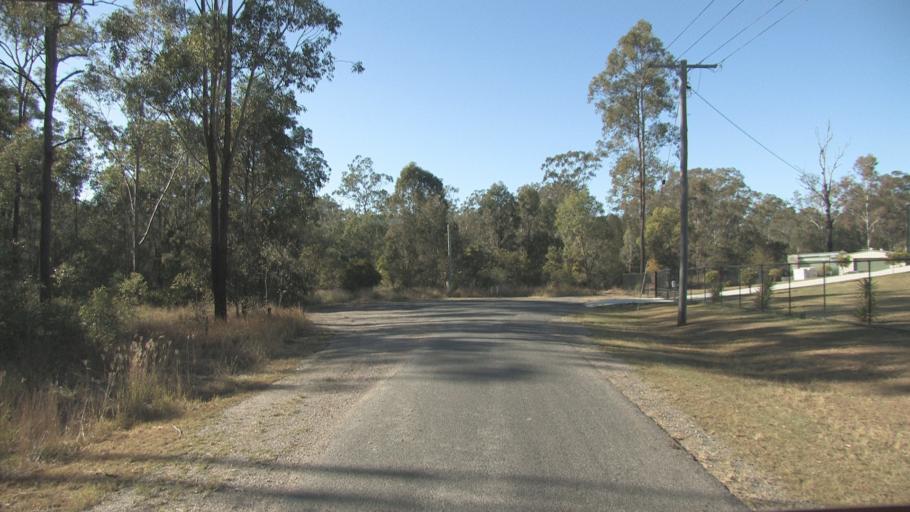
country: AU
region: Queensland
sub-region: Logan
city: Park Ridge South
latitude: -27.7537
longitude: 153.0414
